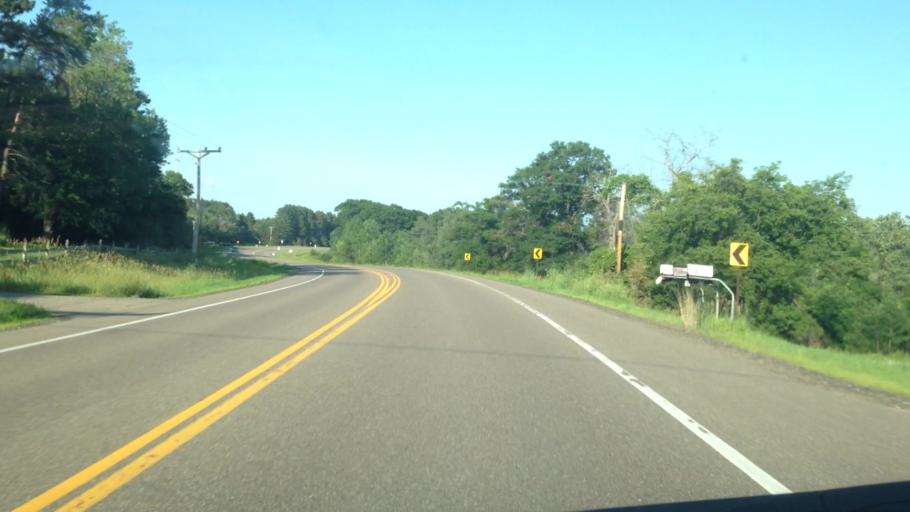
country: US
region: Minnesota
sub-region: Sherburne County
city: Zimmerman
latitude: 45.4439
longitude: -93.6440
